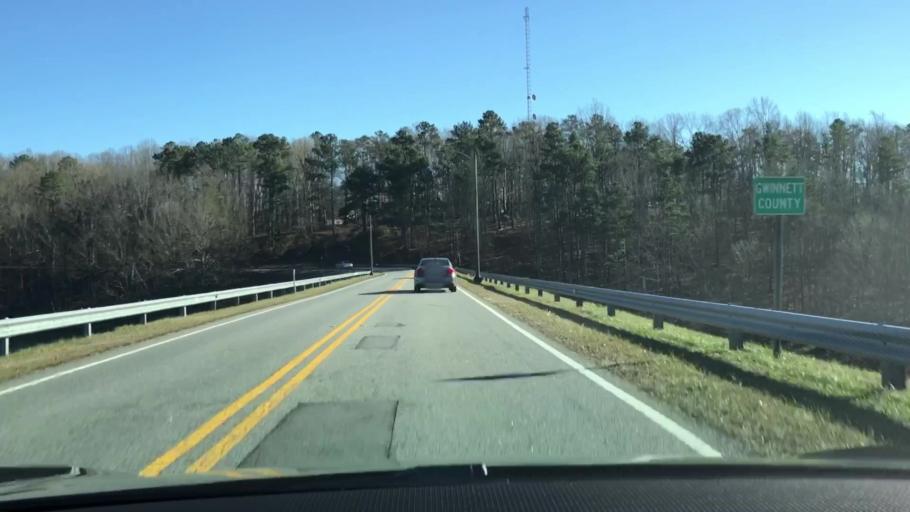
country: US
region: Georgia
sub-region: Gwinnett County
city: Sugar Hill
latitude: 34.1594
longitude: -84.0733
